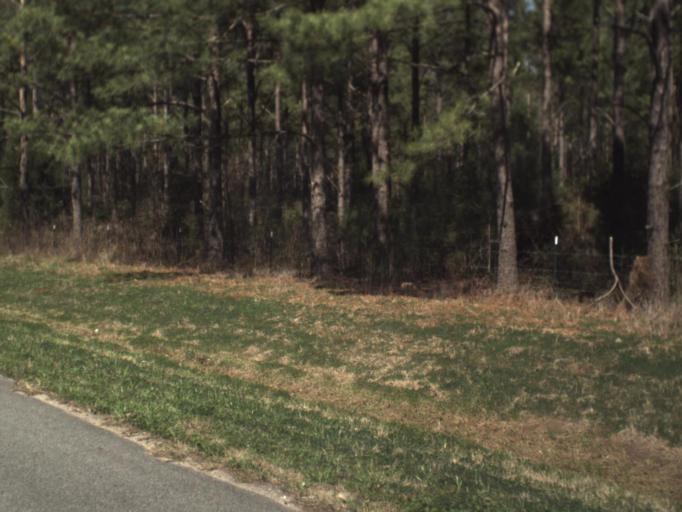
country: US
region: Florida
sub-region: Jackson County
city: Marianna
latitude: 30.8331
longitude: -85.3377
